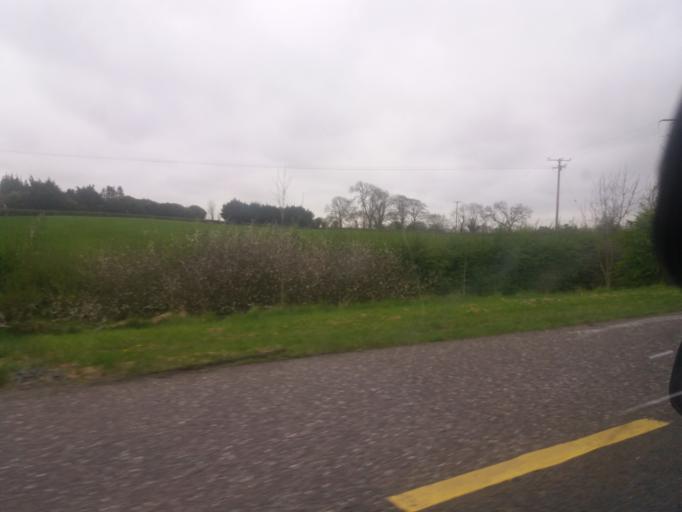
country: IE
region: Munster
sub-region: County Limerick
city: Adare
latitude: 52.5784
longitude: -8.7543
